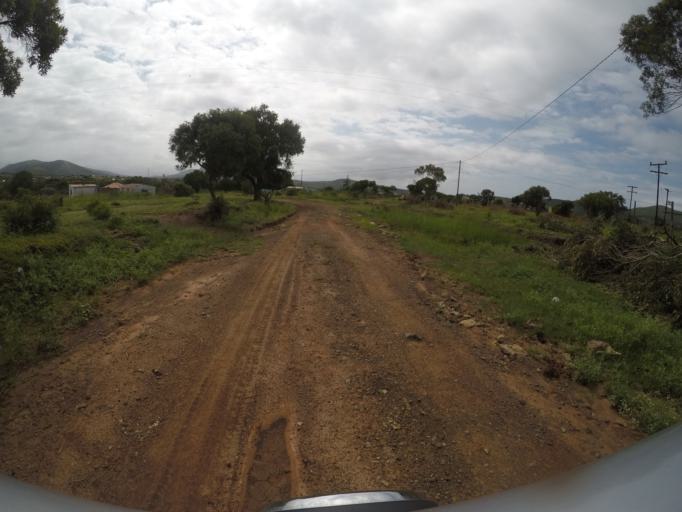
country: ZA
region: KwaZulu-Natal
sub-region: uThungulu District Municipality
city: Empangeni
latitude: -28.6151
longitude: 31.8499
